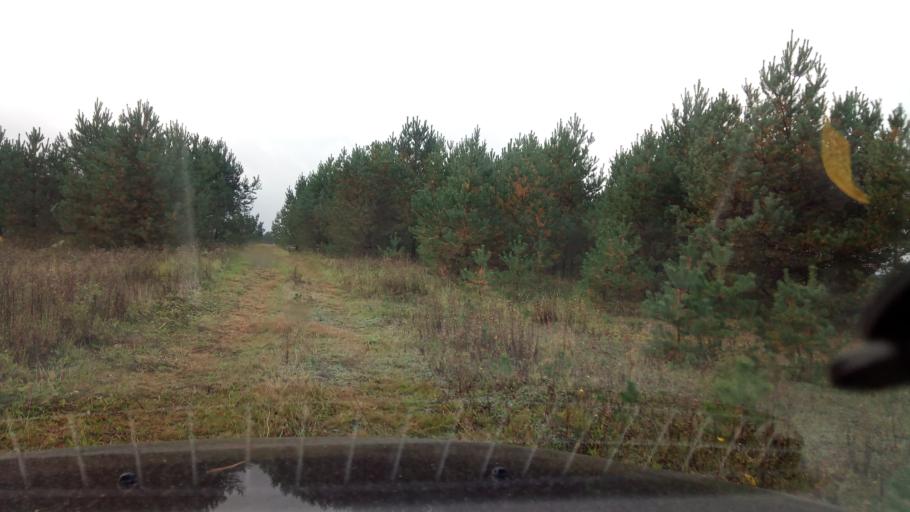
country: LT
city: Skaidiskes
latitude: 54.6210
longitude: 25.5200
